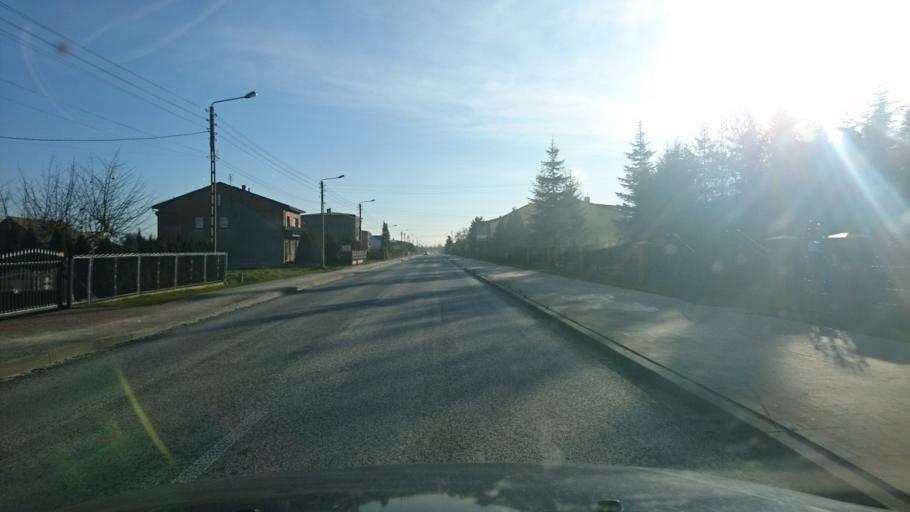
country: PL
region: Silesian Voivodeship
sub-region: Powiat klobucki
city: Starokrzepice
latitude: 51.0129
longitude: 18.6555
